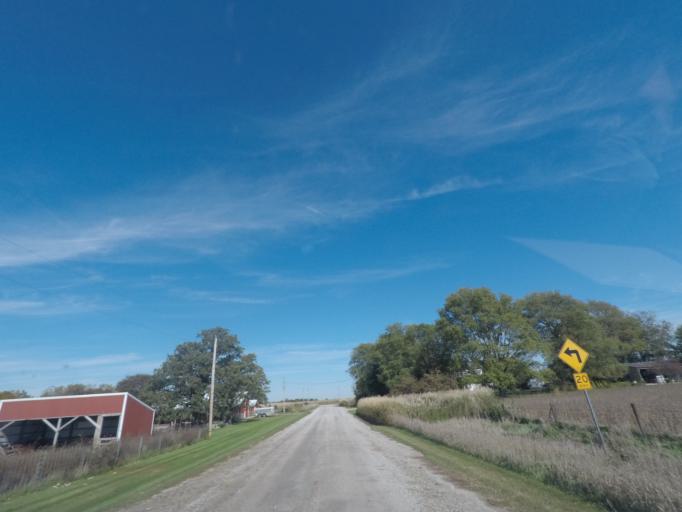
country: US
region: Iowa
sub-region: Story County
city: Nevada
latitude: 42.0435
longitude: -93.3595
